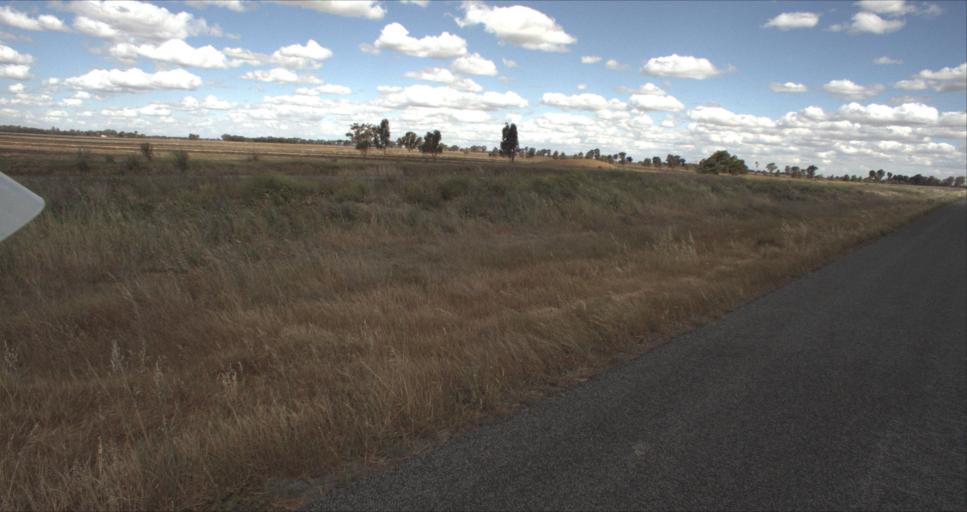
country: AU
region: New South Wales
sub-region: Leeton
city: Leeton
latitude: -34.4512
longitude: 146.2546
